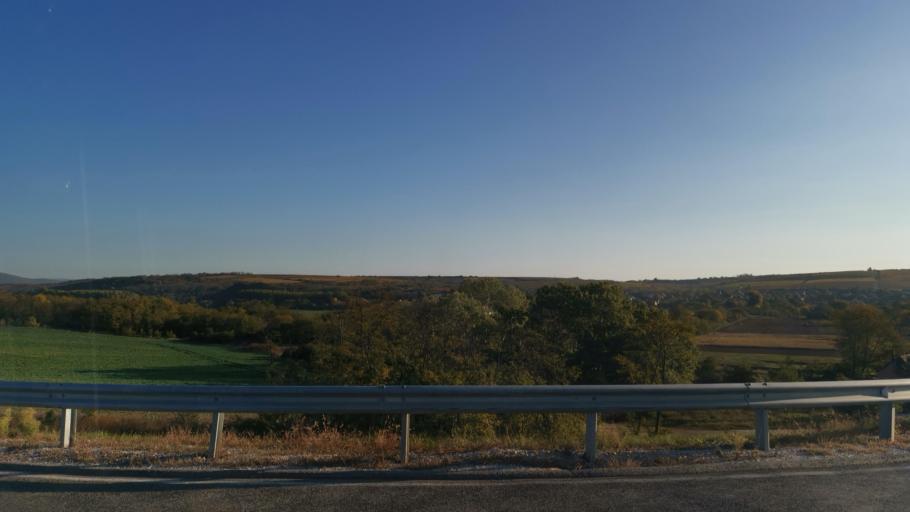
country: HU
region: Heves
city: Andornaktalya
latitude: 47.8390
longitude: 20.4015
